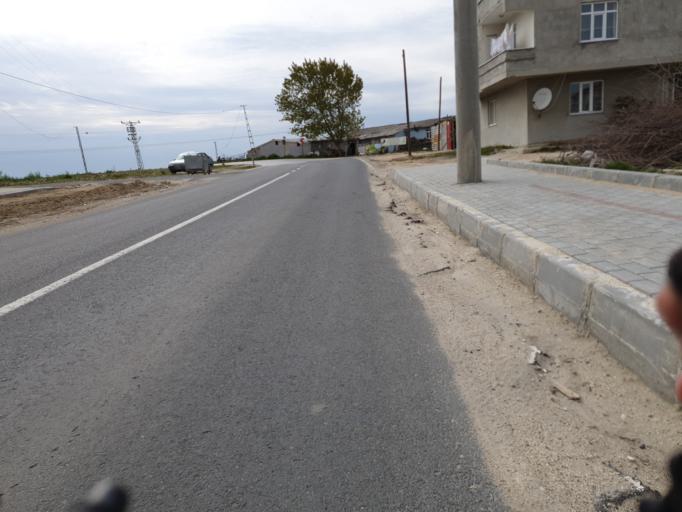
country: TR
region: Tekirdag
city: Cerkezkoey
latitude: 41.2944
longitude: 27.9343
